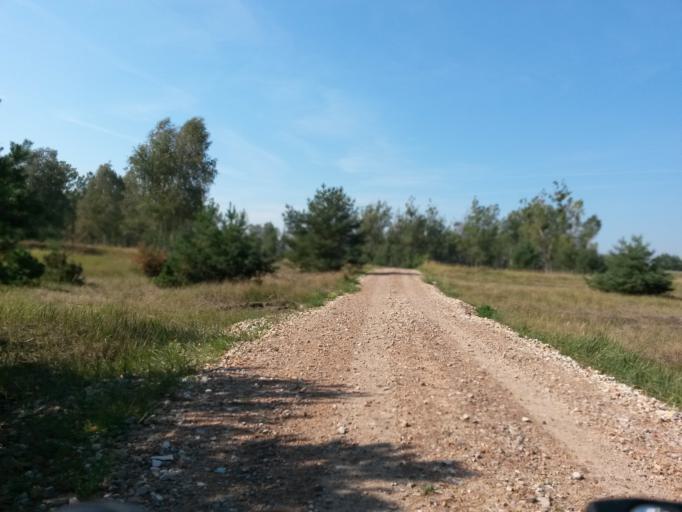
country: DE
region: Brandenburg
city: Zehdenick
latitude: 53.0637
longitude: 13.3741
